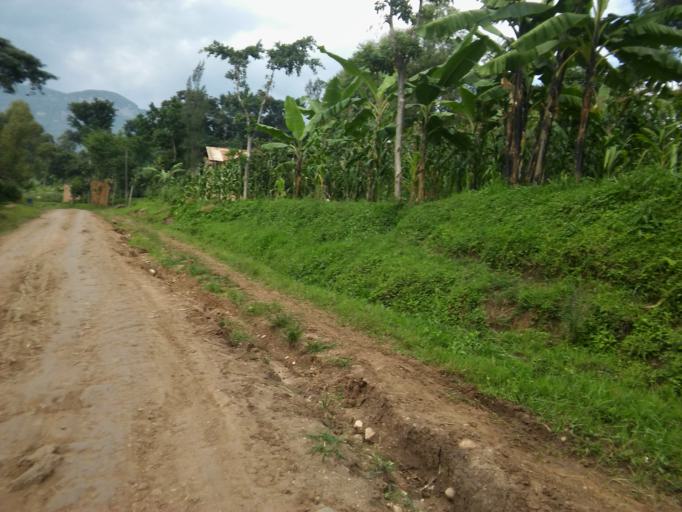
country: UG
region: Eastern Region
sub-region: Manafwa District
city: Manafwa
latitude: 0.8916
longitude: 34.3604
